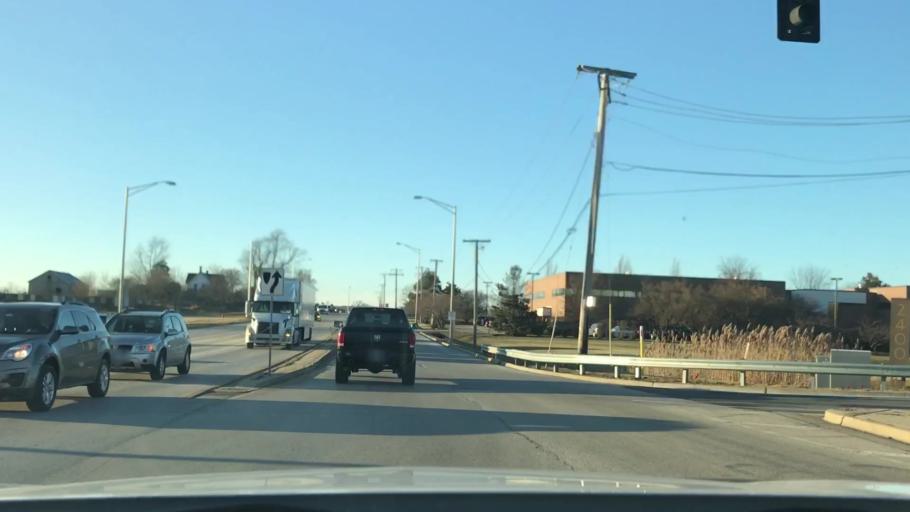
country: US
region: Illinois
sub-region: Kane County
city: Sleepy Hollow
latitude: 42.0651
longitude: -88.3358
